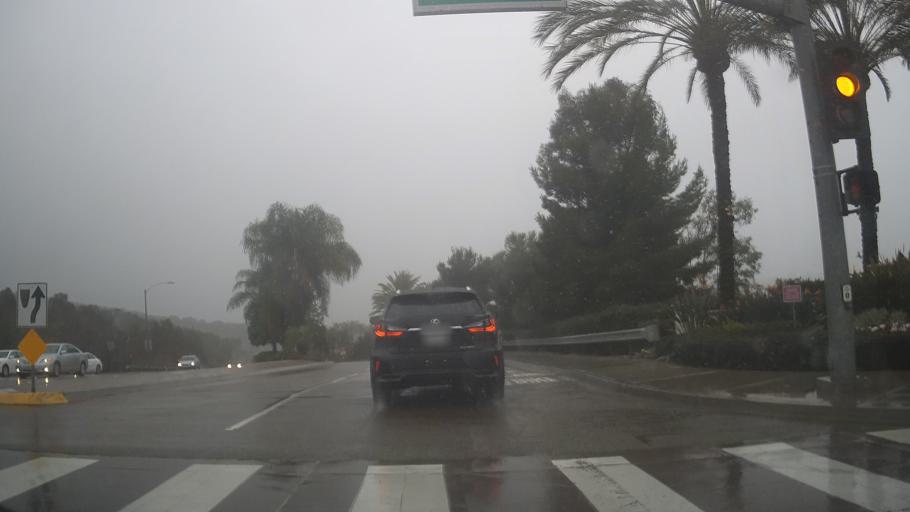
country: US
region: California
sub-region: San Diego County
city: Encinitas
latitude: 33.0687
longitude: -117.2675
